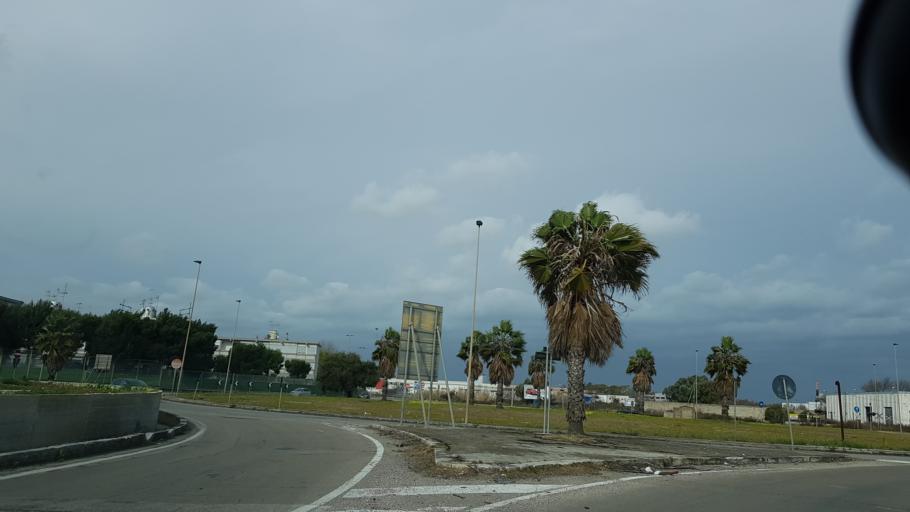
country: IT
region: Apulia
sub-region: Provincia di Brindisi
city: La Rosa
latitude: 40.6277
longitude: 17.9619
